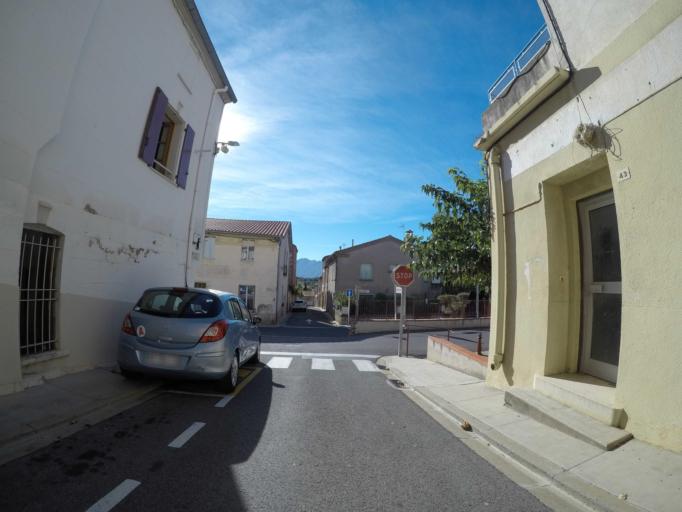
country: FR
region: Languedoc-Roussillon
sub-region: Departement des Pyrenees-Orientales
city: Villemolaque
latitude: 42.5780
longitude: 2.8115
